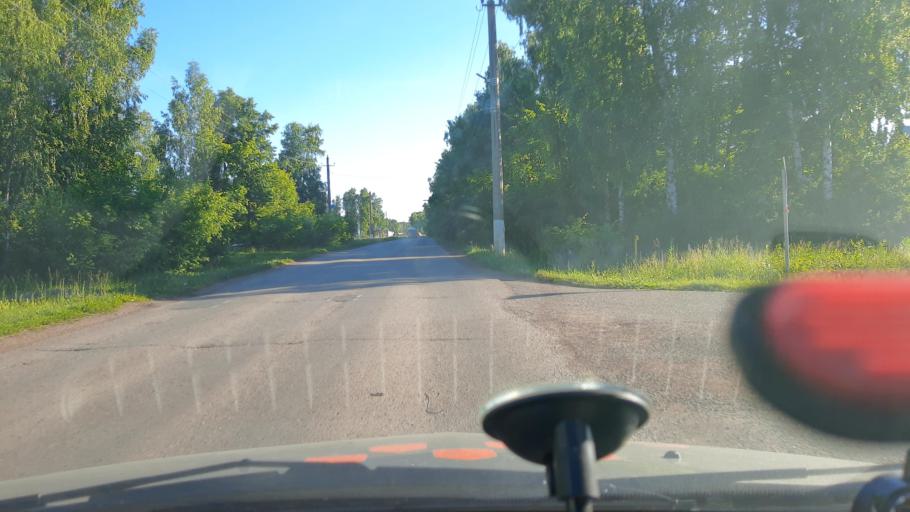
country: RU
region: Bashkortostan
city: Chishmy
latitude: 54.5948
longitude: 55.3676
